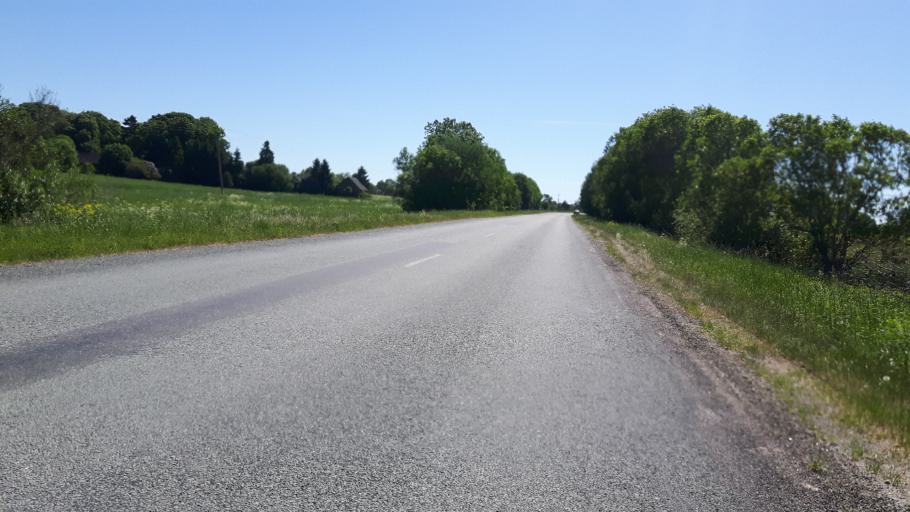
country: EE
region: Harju
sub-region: Kuusalu vald
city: Kuusalu
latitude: 59.5097
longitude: 25.5199
